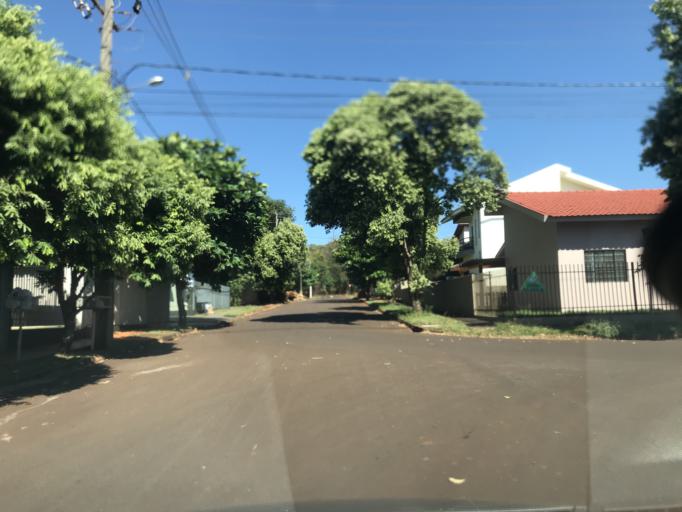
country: BR
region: Parana
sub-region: Palotina
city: Palotina
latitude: -24.2784
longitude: -53.8265
